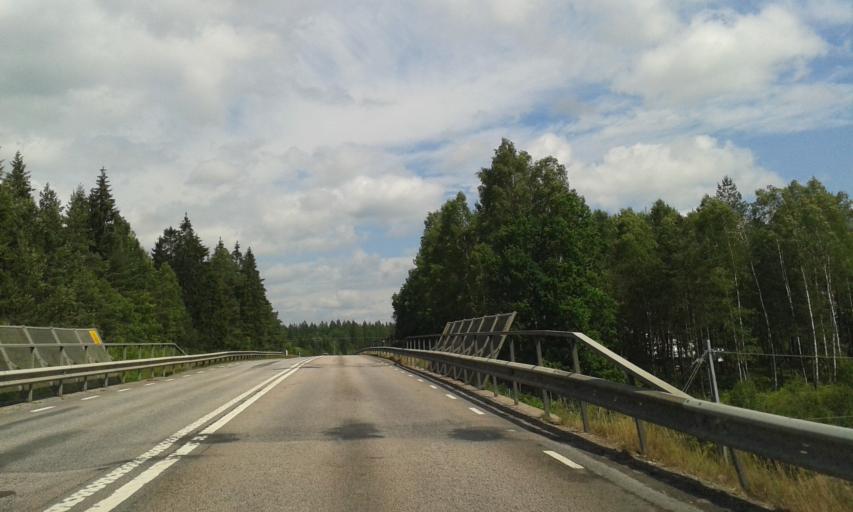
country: SE
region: Kronoberg
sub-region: Alvesta Kommun
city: Alvesta
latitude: 56.9102
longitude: 14.4774
